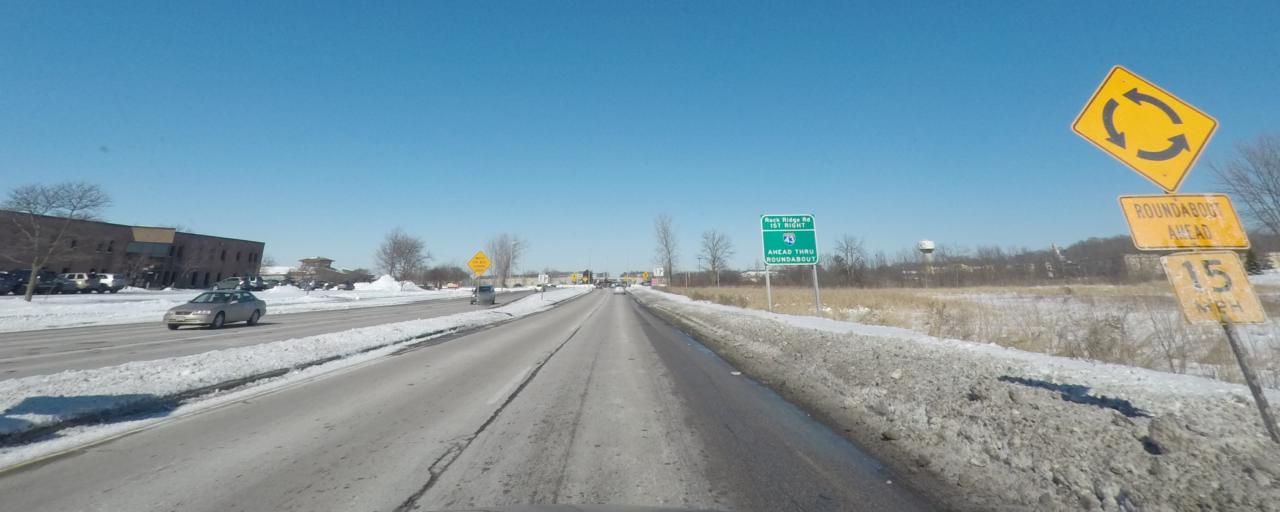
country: US
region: Wisconsin
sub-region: Waukesha County
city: New Berlin
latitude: 42.9468
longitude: -88.1089
